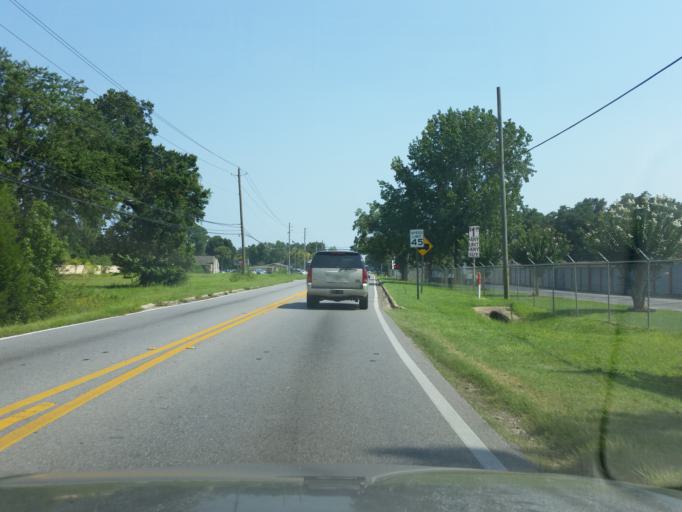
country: US
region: Florida
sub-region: Escambia County
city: Brent
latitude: 30.4795
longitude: -87.2471
